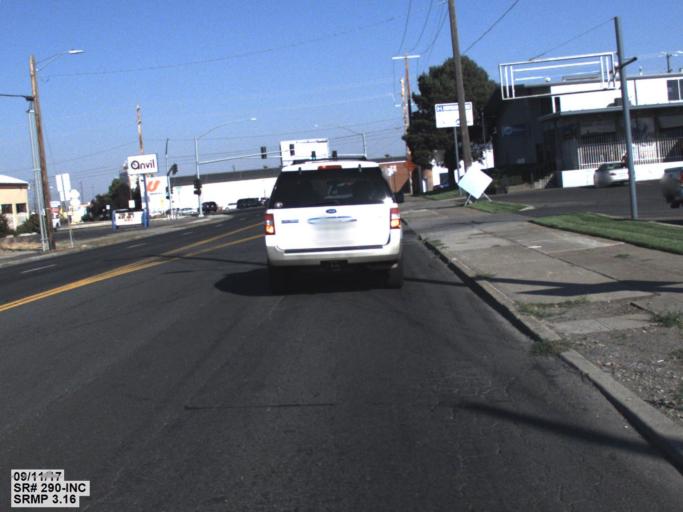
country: US
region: Washington
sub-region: Spokane County
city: Millwood
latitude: 47.6709
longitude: -117.3481
